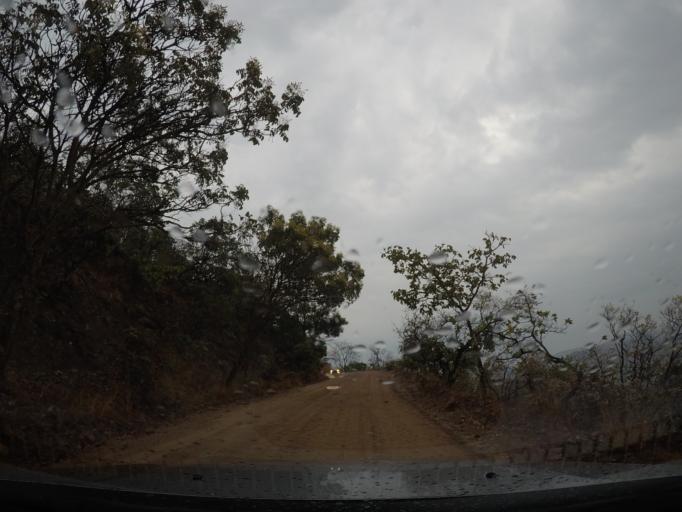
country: BR
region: Goias
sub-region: Pirenopolis
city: Pirenopolis
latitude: -15.8190
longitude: -48.9009
